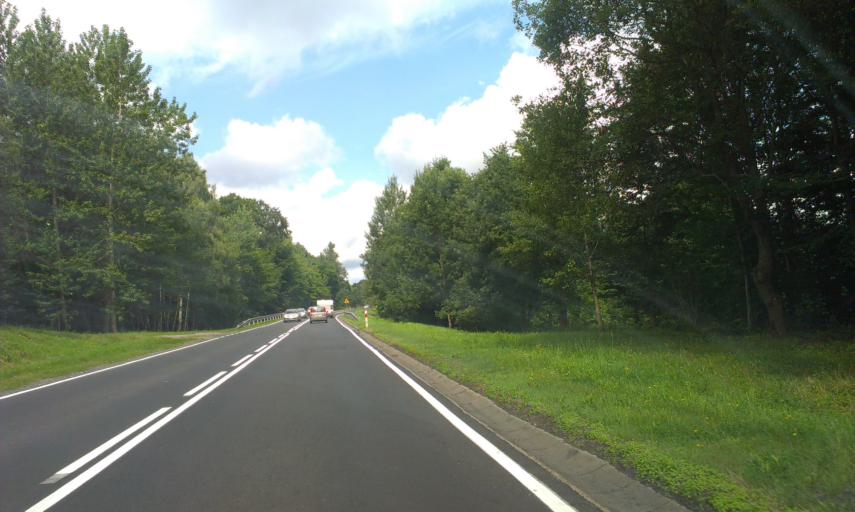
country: PL
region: West Pomeranian Voivodeship
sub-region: Powiat koszalinski
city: Bobolice
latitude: 53.9856
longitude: 16.5404
